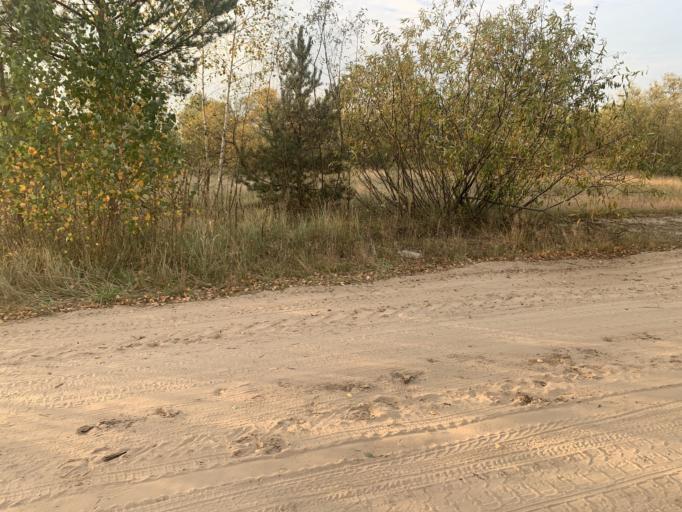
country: BY
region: Brest
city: Mikashevichy
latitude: 52.3323
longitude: 27.4978
